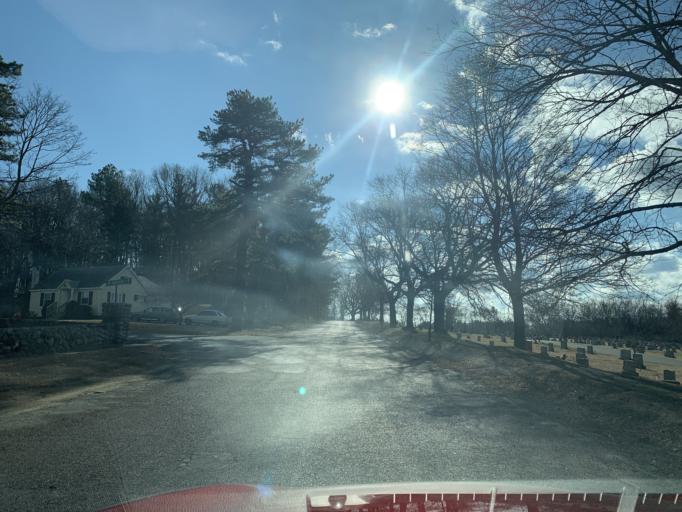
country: US
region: Massachusetts
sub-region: Essex County
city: Amesbury
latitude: 42.8432
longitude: -70.9339
